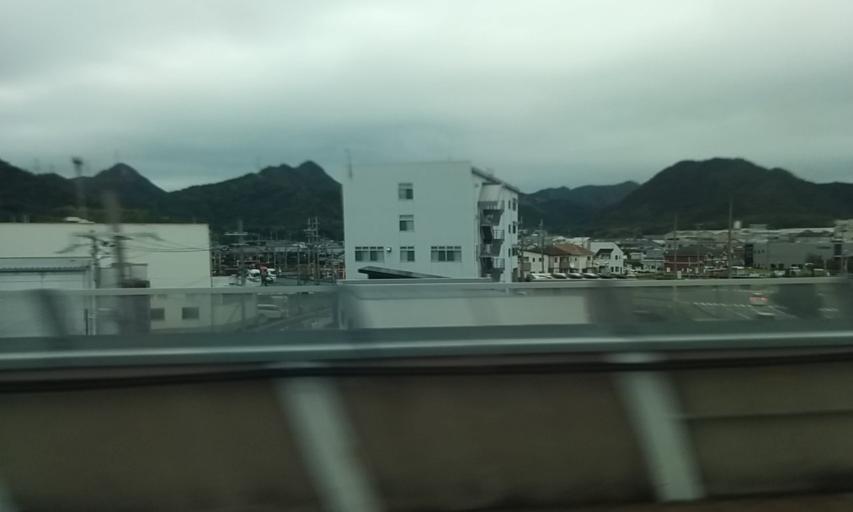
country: JP
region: Hyogo
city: Shirahamacho-usazakiminami
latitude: 34.8028
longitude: 134.7529
